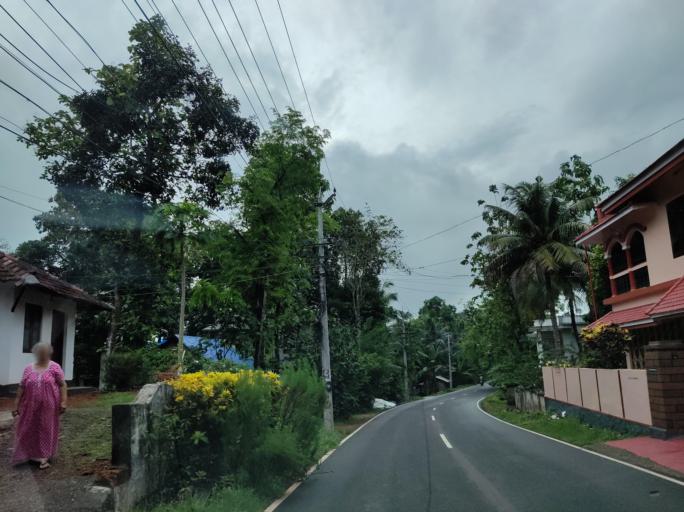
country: IN
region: Kerala
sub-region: Alappuzha
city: Mavelikara
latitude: 9.2308
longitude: 76.5641
